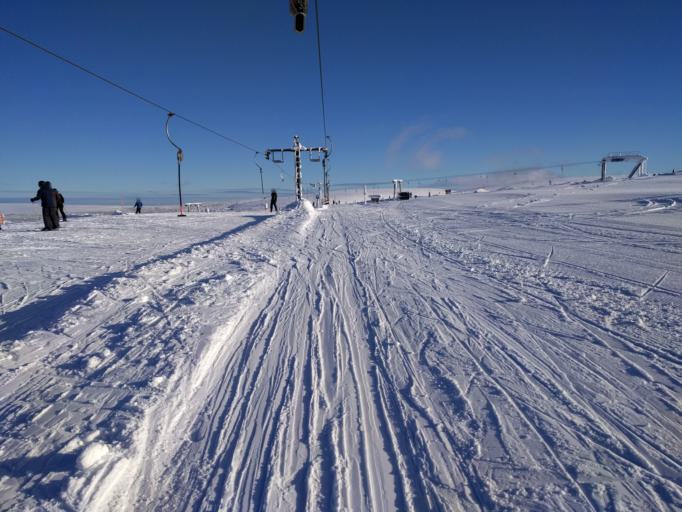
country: NO
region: Hedmark
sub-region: Trysil
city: Innbygda
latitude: 61.1737
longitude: 13.0230
